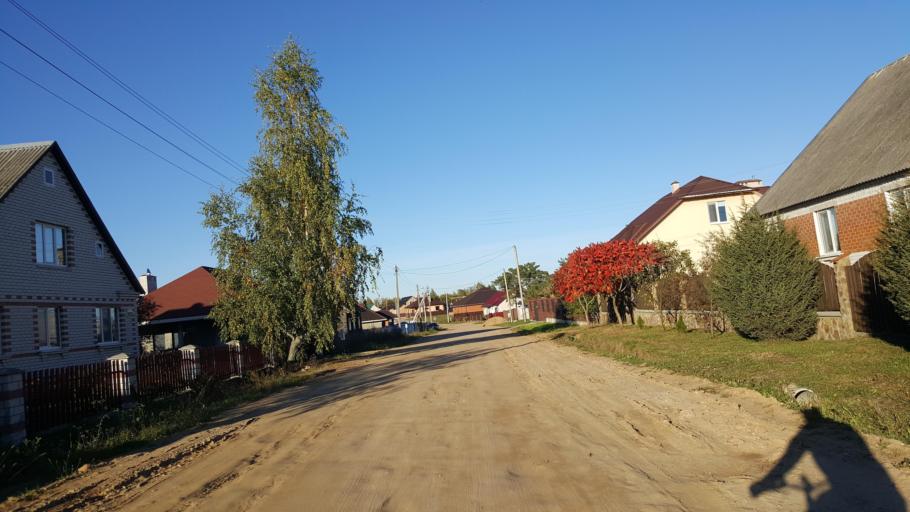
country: BY
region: Brest
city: Kamyanyets
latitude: 52.3995
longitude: 23.8441
